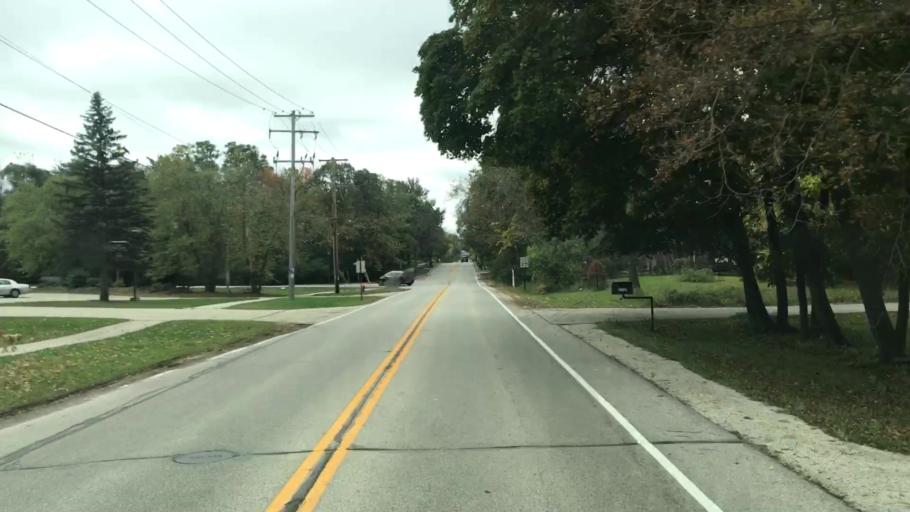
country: US
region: Wisconsin
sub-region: Waukesha County
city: Brookfield
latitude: 43.0769
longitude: -88.1459
